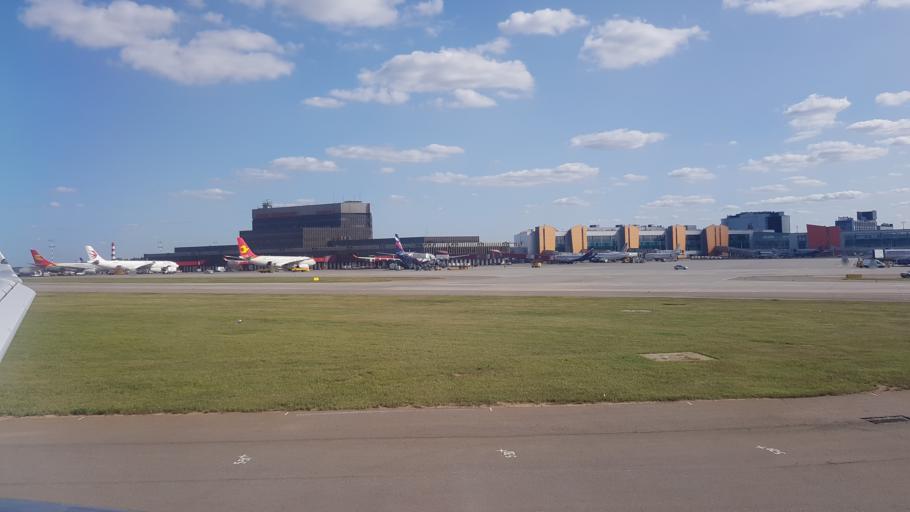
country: RU
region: Moskovskaya
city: Novopodrezkovo
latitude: 55.9693
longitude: 37.4091
